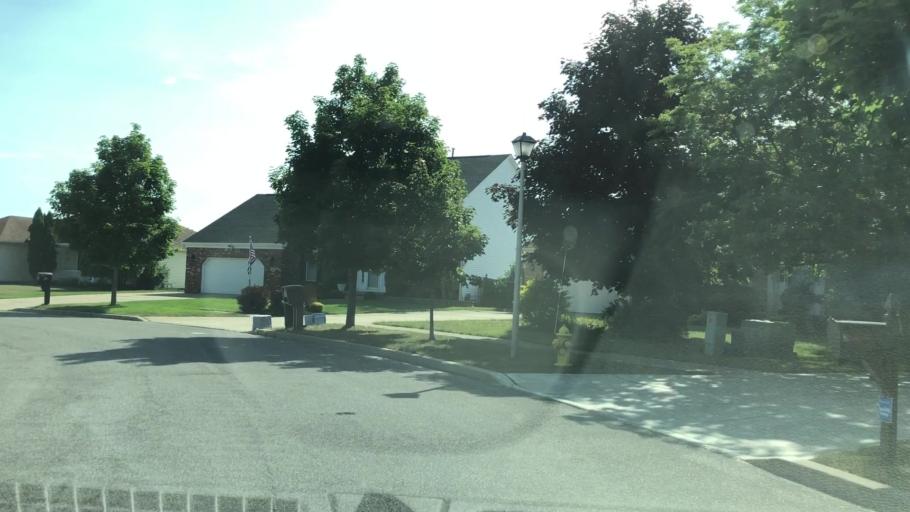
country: US
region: New York
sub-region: Erie County
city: Lancaster
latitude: 42.8776
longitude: -78.6843
